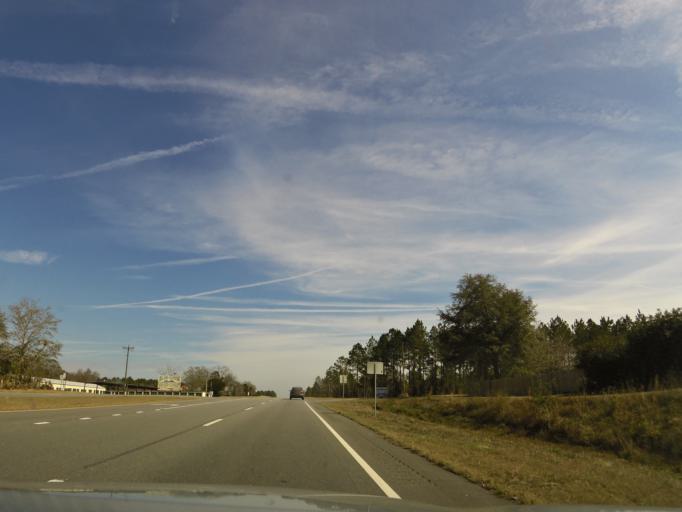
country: US
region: Georgia
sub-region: Brantley County
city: Nahunta
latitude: 31.2158
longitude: -81.8929
